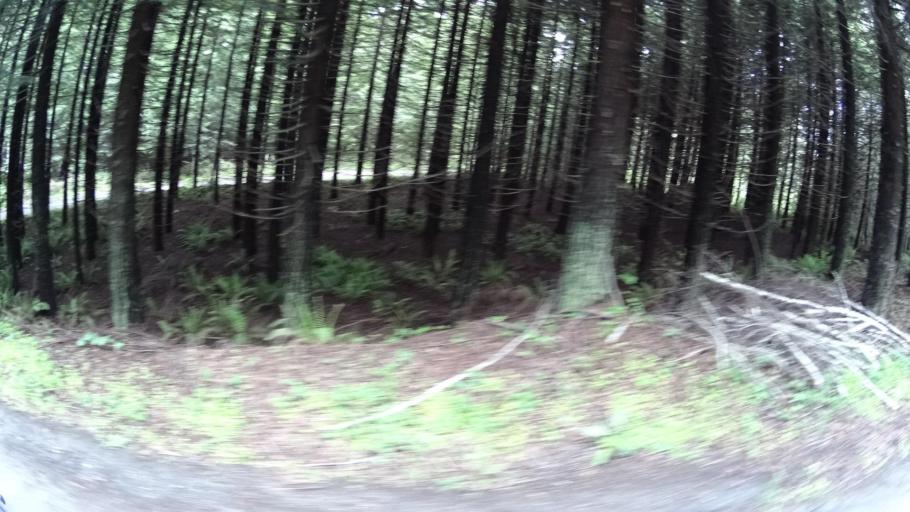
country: US
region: California
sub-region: Humboldt County
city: Blue Lake
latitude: 40.9078
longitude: -123.9747
